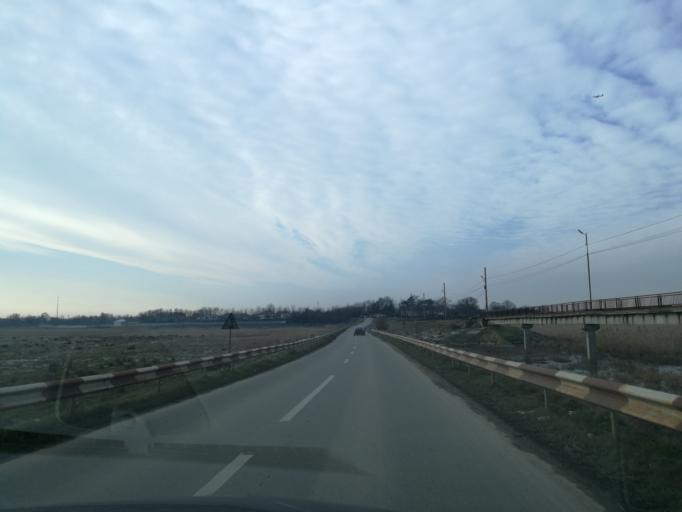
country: RO
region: Ialomita
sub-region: Comuna Fierbinti-Targ
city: Fierbintii de Jos
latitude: 44.6879
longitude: 26.3910
